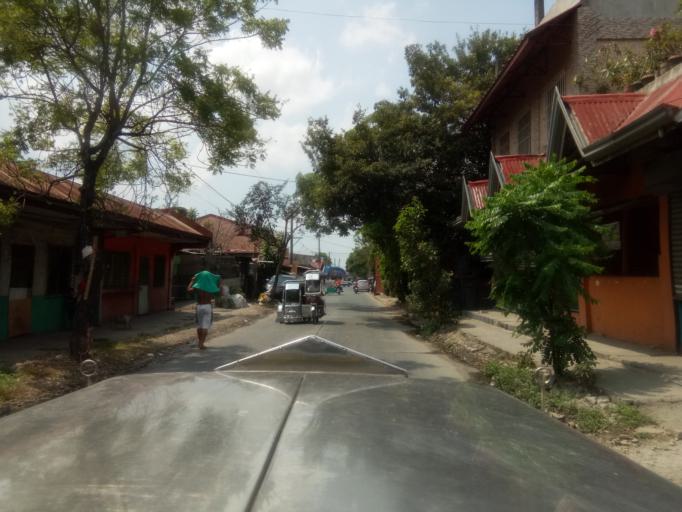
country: PH
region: Calabarzon
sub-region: Province of Cavite
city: Dasmarinas
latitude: 14.3172
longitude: 120.9765
